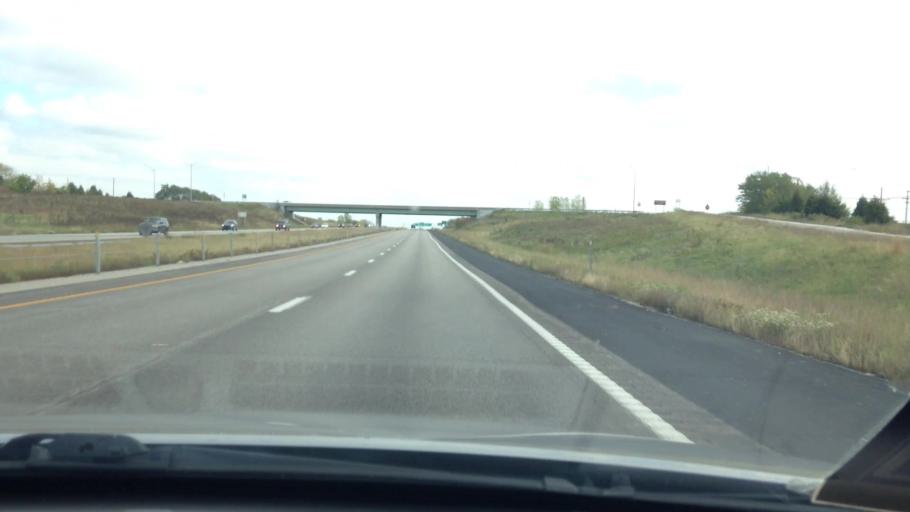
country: US
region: Missouri
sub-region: Clay County
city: Gladstone
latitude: 39.2552
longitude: -94.6043
